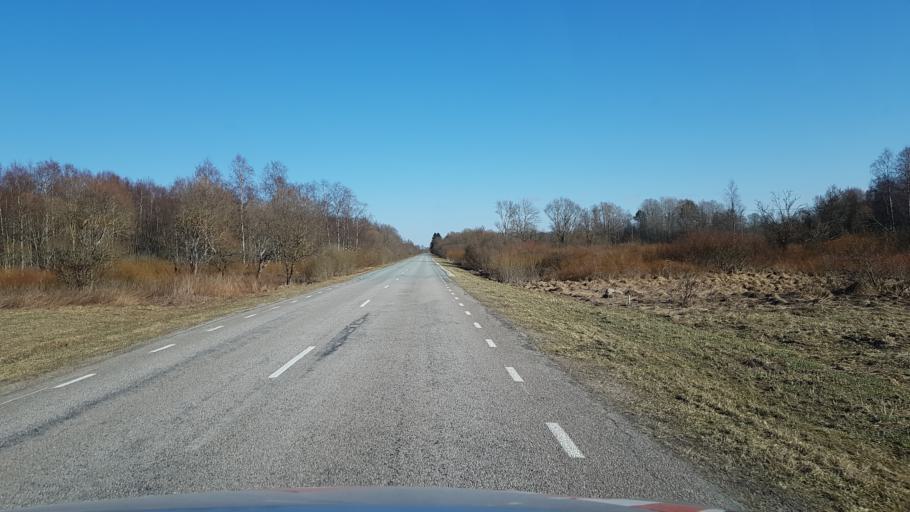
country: EE
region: Laeaene-Virumaa
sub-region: Haljala vald
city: Haljala
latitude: 59.5082
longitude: 26.1108
